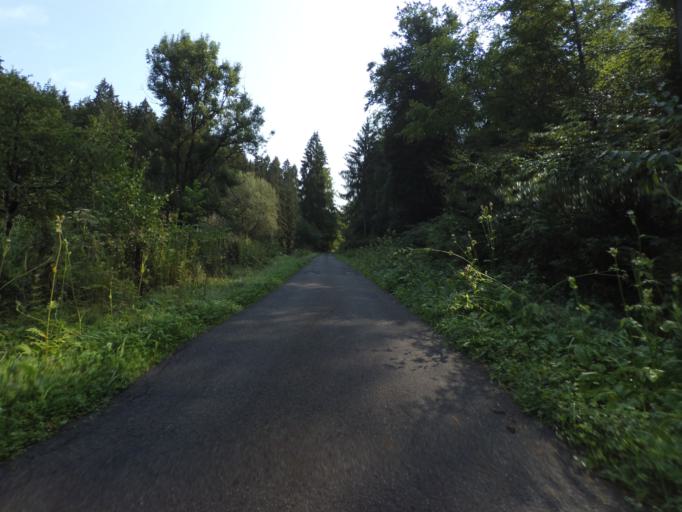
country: DE
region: Saarland
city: Orscholz
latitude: 49.4768
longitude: 6.5199
